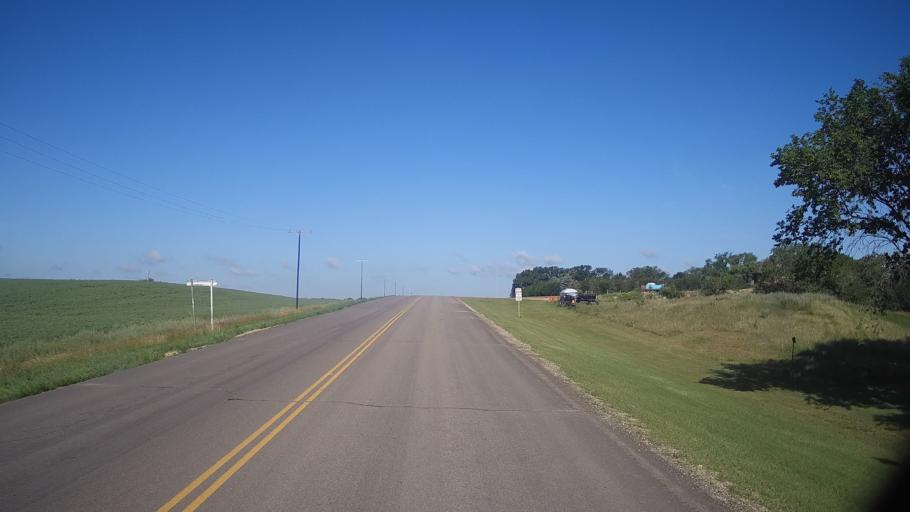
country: CA
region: Saskatchewan
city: Watrous
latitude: 51.6781
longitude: -105.4052
